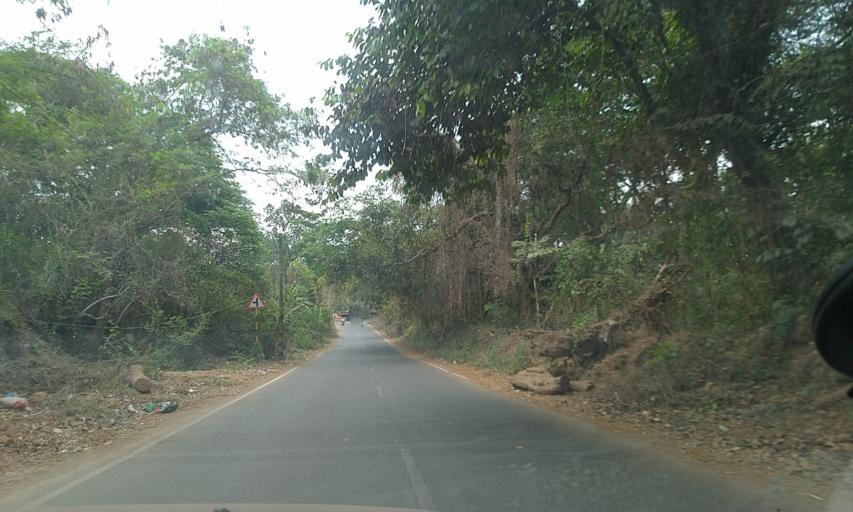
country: IN
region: Goa
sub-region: North Goa
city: Jua
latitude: 15.4958
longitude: 73.9122
